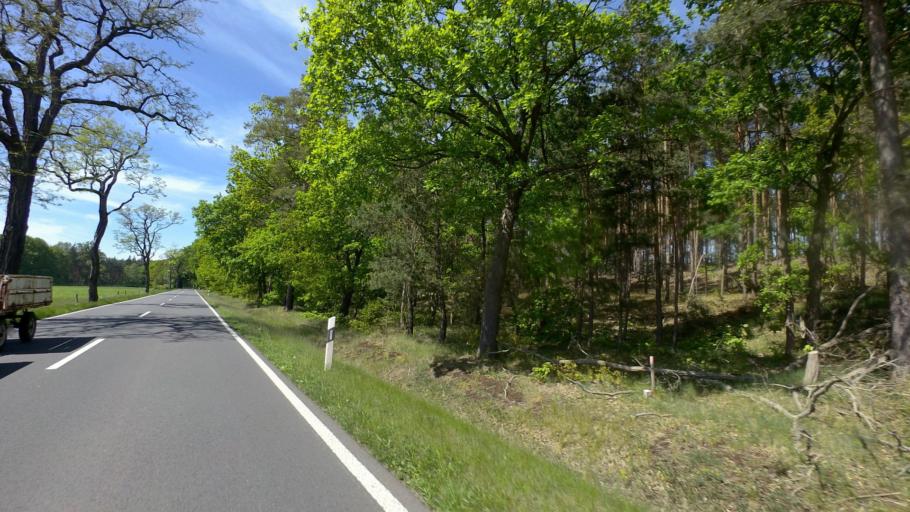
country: DE
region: Brandenburg
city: Baruth
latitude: 52.0649
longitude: 13.4830
